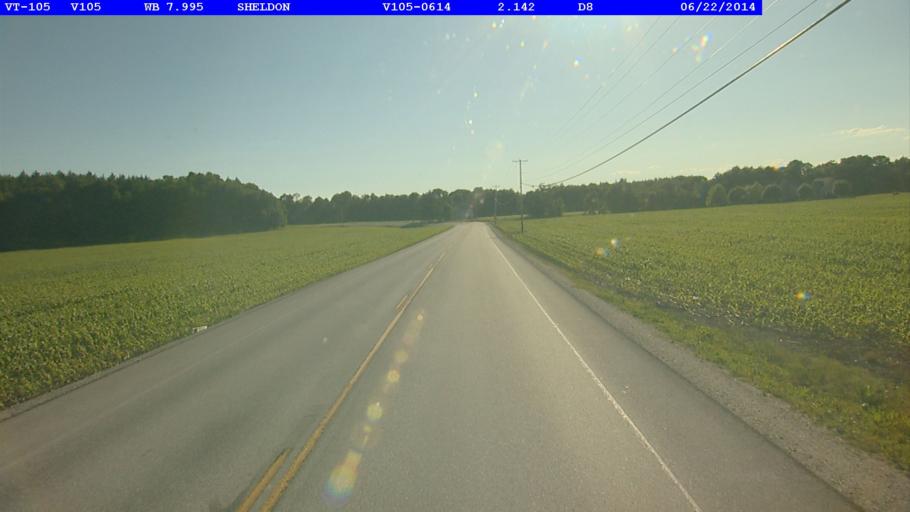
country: US
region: Vermont
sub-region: Franklin County
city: Saint Albans
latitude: 44.9049
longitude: -72.9894
